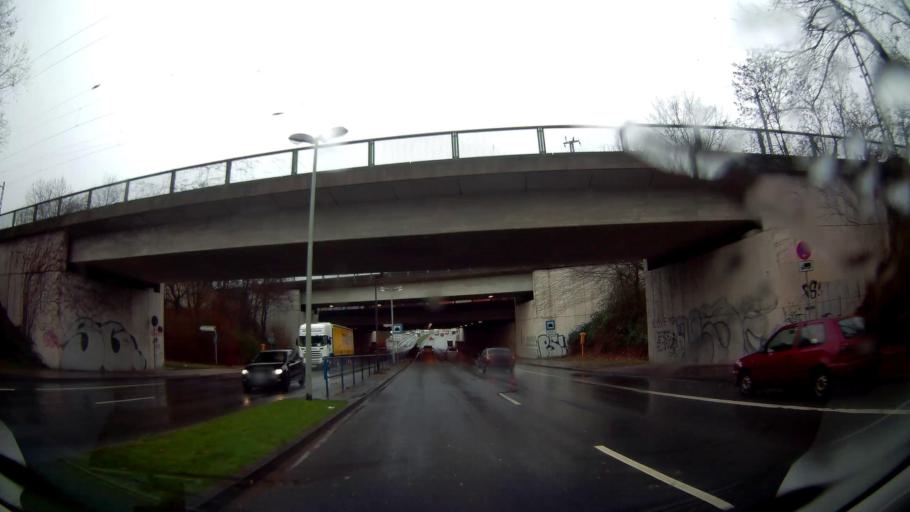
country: DE
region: North Rhine-Westphalia
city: Bochum-Hordel
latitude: 51.5376
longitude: 7.1810
